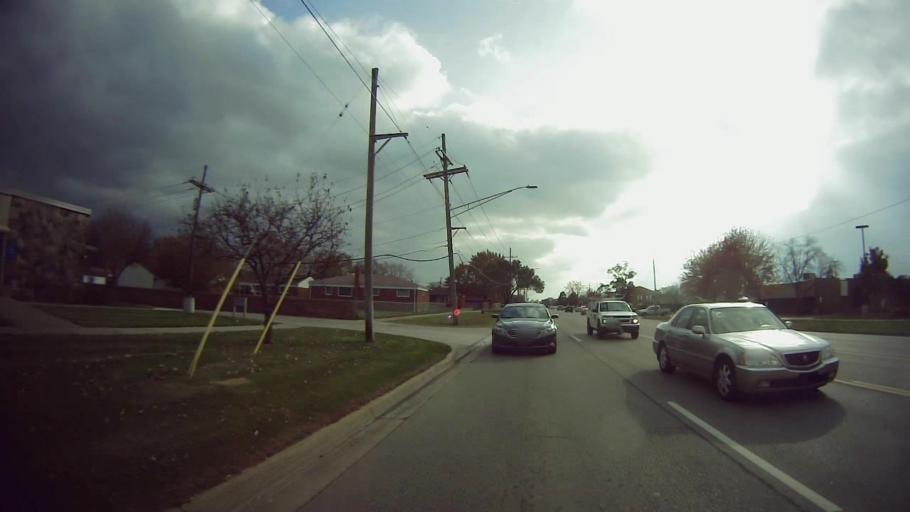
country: US
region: Michigan
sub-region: Macomb County
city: Fraser
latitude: 42.5204
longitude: -82.9881
